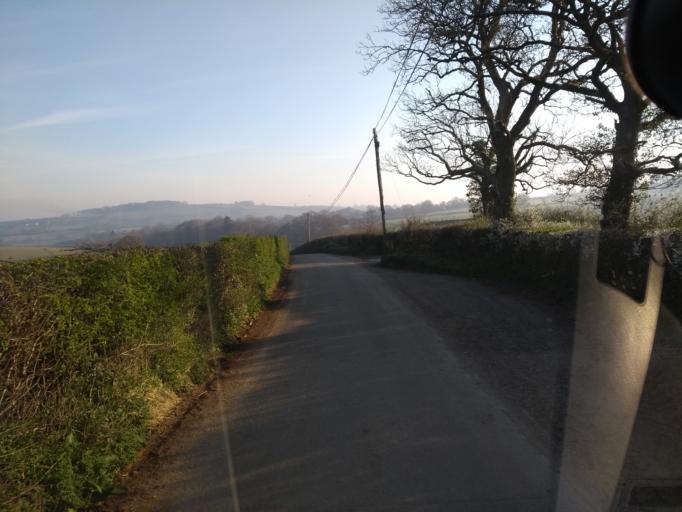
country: GB
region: England
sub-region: Somerset
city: Crewkerne
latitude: 50.8325
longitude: -2.7866
